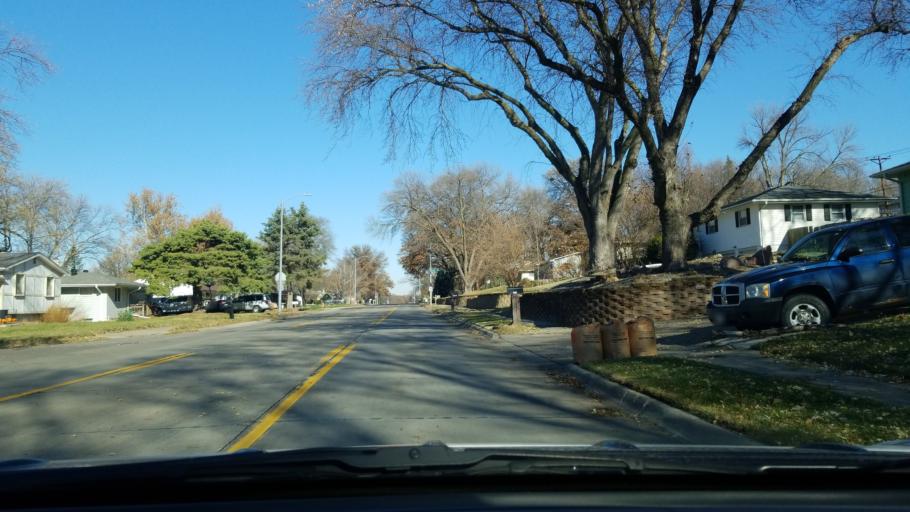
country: US
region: Nebraska
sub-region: Douglas County
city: Ralston
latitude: 41.2275
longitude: -96.0815
